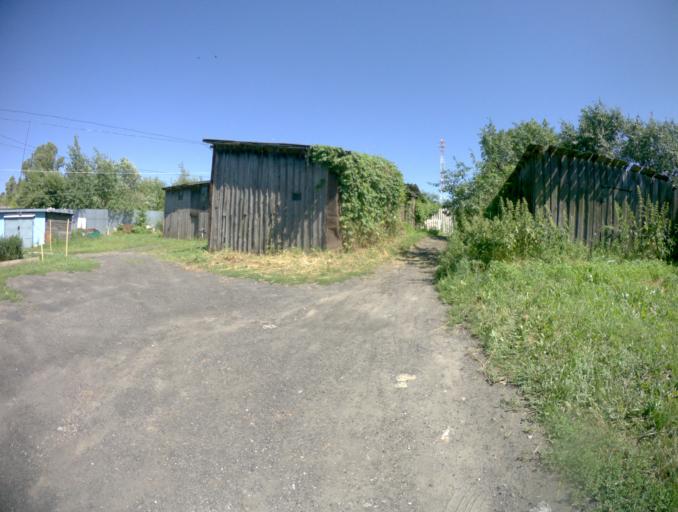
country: RU
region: Nizjnij Novgorod
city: Gorbatov
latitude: 56.1257
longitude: 43.0609
